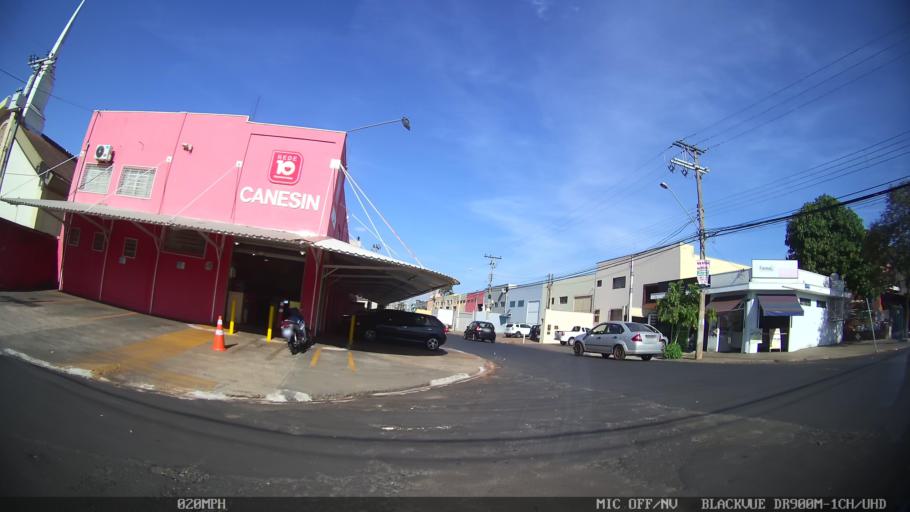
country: BR
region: Sao Paulo
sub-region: Ribeirao Preto
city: Ribeirao Preto
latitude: -21.1758
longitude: -47.7608
